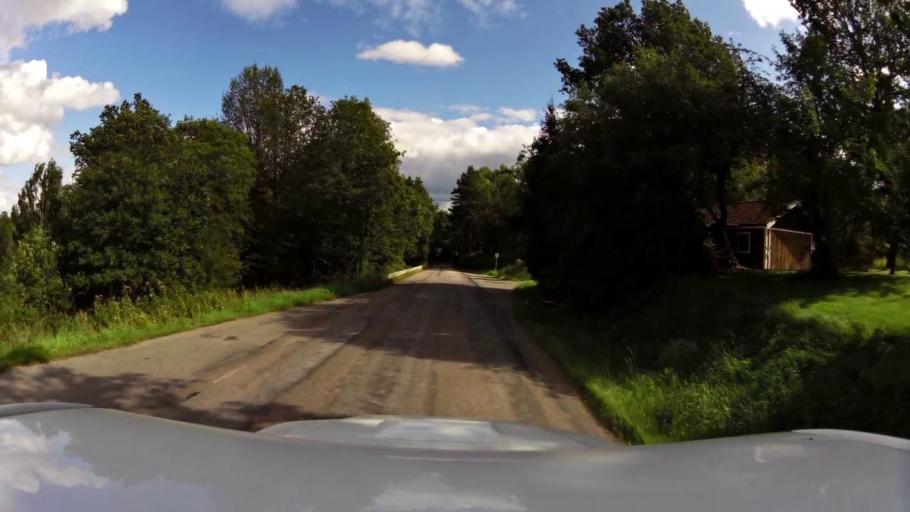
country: SE
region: OEstergoetland
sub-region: Kinda Kommun
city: Rimforsa
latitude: 58.2296
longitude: 15.6962
